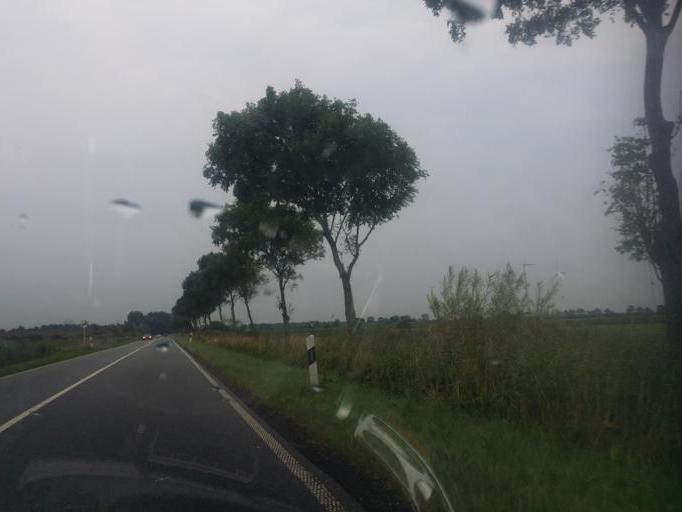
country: DE
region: Schleswig-Holstein
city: Husum
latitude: 54.4612
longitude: 9.0482
